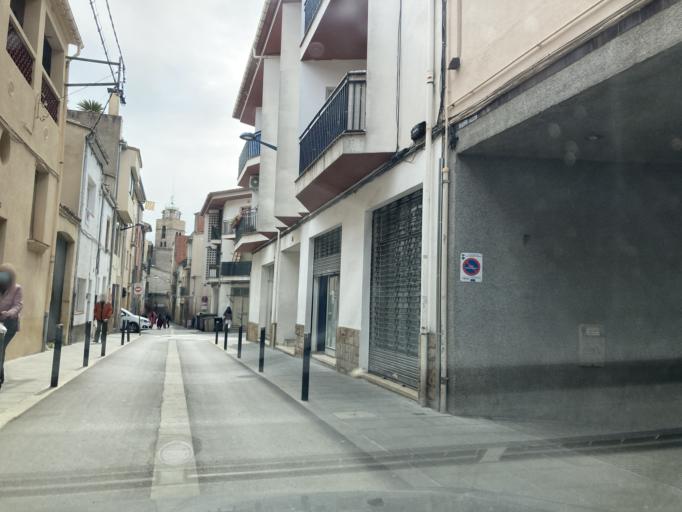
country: ES
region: Catalonia
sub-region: Provincia de Girona
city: Santa Coloma de Farners
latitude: 41.8644
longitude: 2.6611
